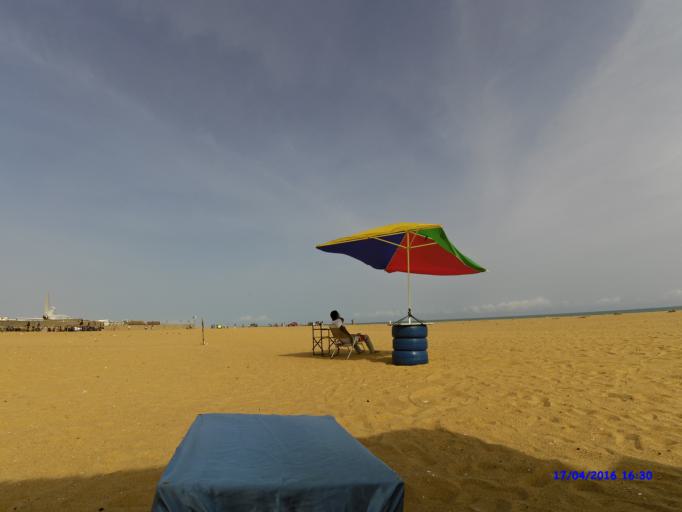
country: BJ
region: Littoral
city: Cotonou
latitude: 6.3474
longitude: 2.3779
